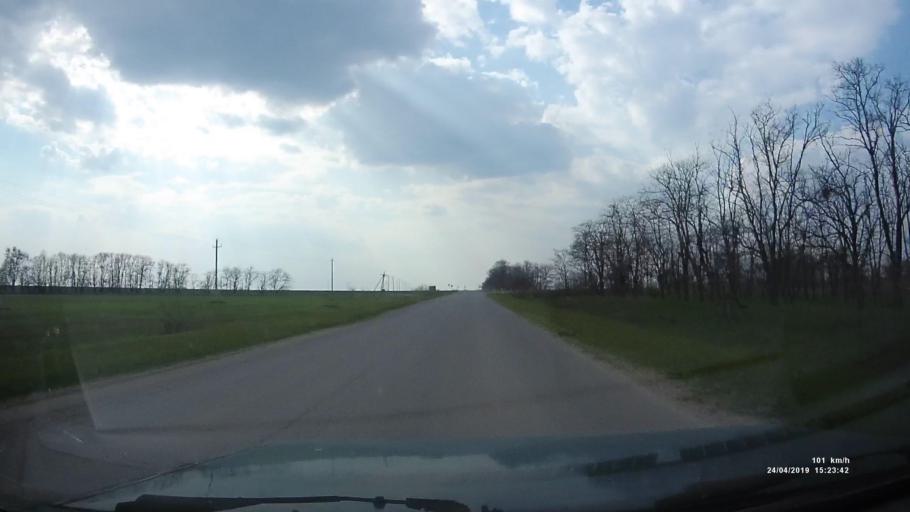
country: RU
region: Rostov
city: Remontnoye
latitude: 46.5446
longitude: 43.0843
